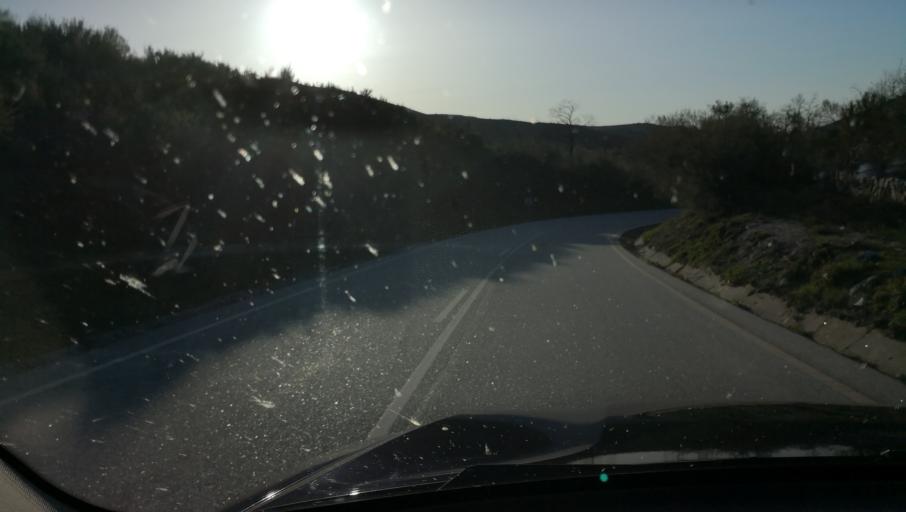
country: PT
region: Vila Real
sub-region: Vila Real
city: Vila Real
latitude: 41.3646
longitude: -7.8000
